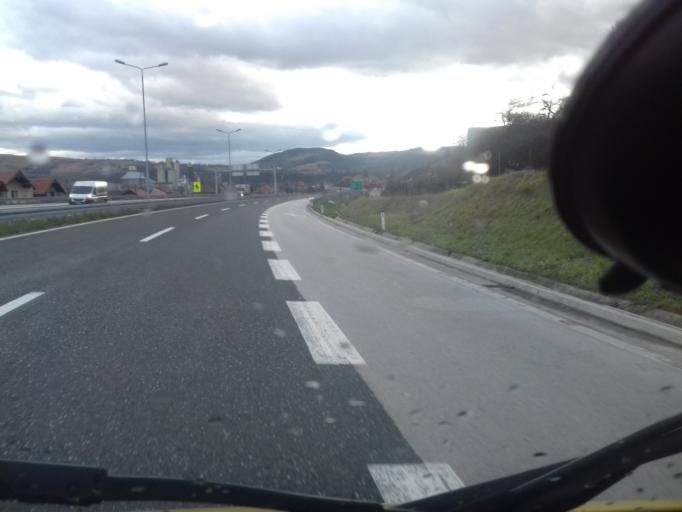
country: BA
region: Federation of Bosnia and Herzegovina
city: Kakanj
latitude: 44.1228
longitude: 18.1004
